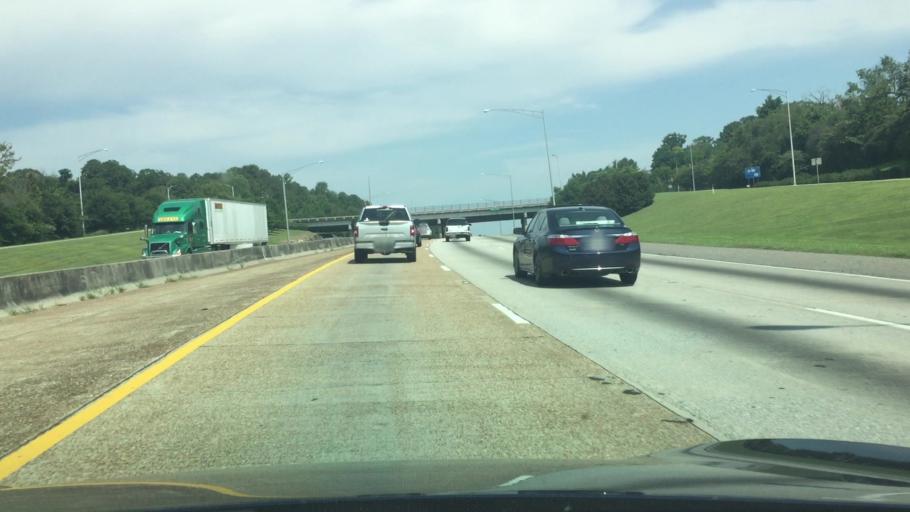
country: US
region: Alabama
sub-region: Jefferson County
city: Hoover
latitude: 33.4295
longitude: -86.8219
